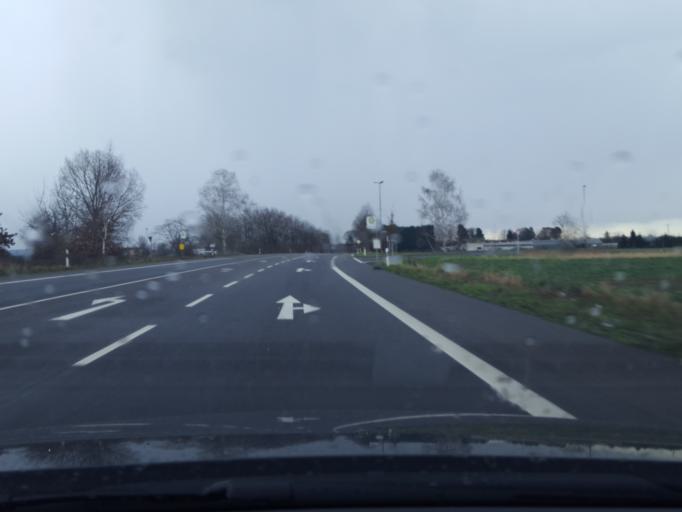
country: DE
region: North Rhine-Westphalia
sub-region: Regierungsbezirk Koln
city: Bonn
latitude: 50.7831
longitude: 7.0888
